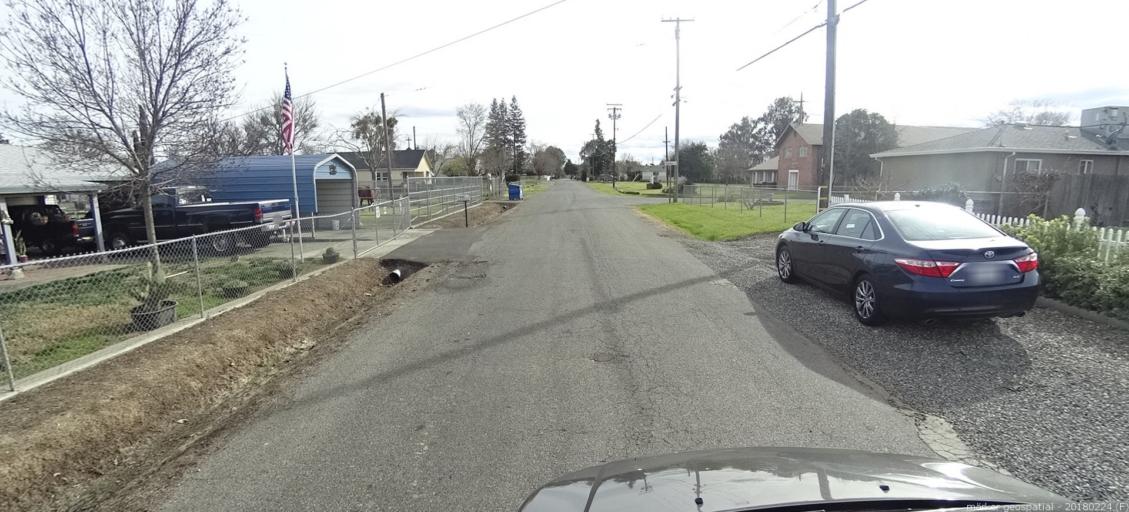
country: US
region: California
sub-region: Sacramento County
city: Elverta
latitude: 38.7127
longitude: -121.4591
